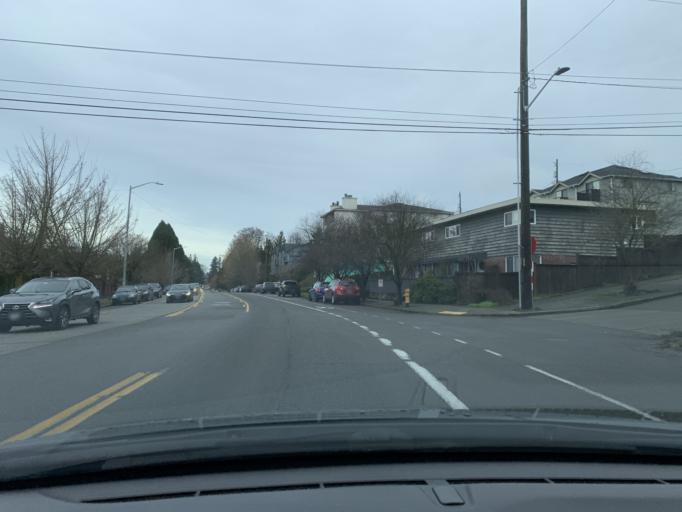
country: US
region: Washington
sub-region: King County
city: White Center
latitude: 47.5465
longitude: -122.3832
